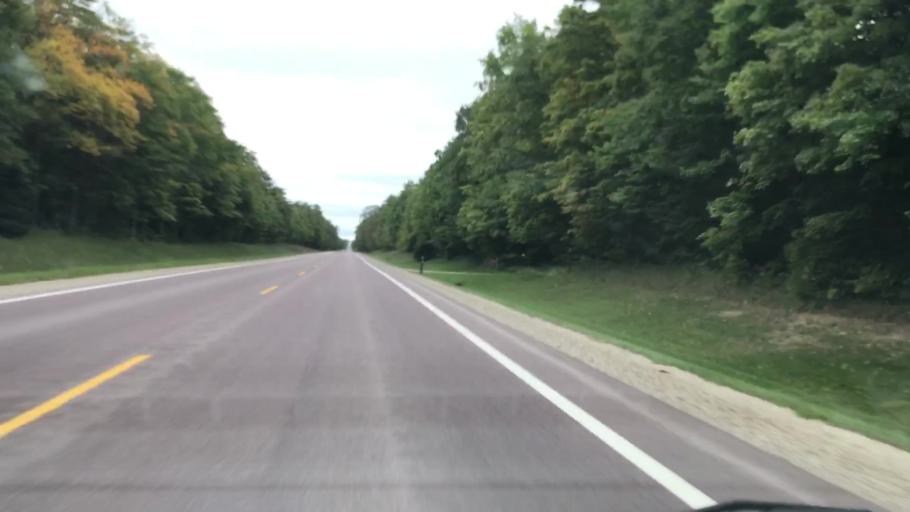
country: US
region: Michigan
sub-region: Luce County
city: Newberry
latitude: 46.2529
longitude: -85.5725
